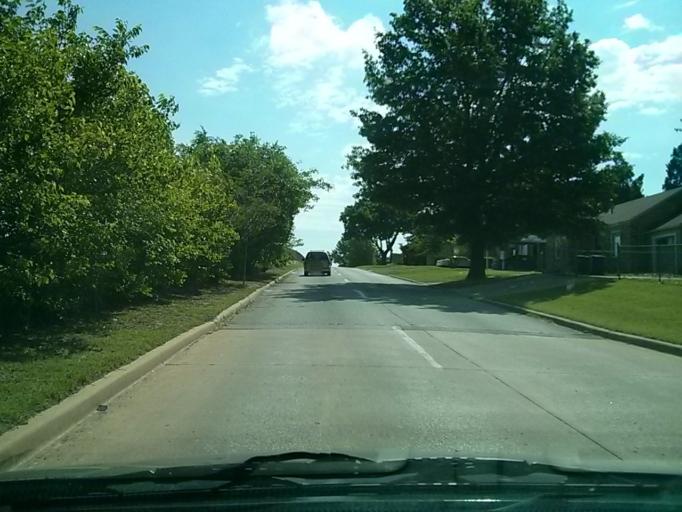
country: US
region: Oklahoma
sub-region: Tulsa County
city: Tulsa
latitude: 36.1591
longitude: -95.9438
